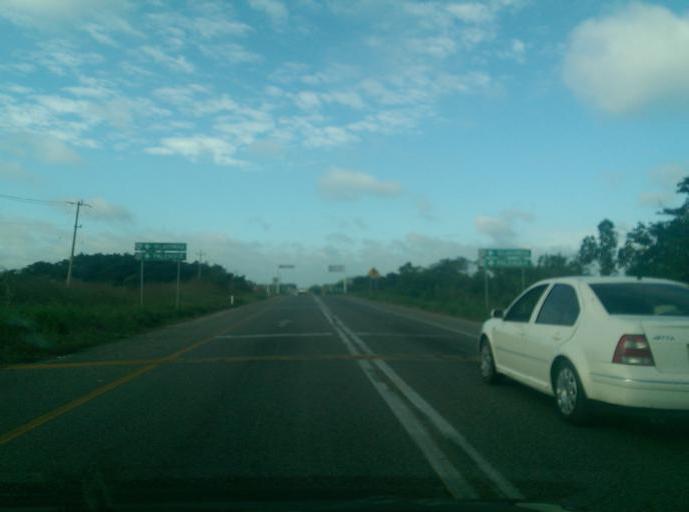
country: MX
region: Chiapas
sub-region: Catazaja
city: Catazaja
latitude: 17.7102
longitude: -92.0168
